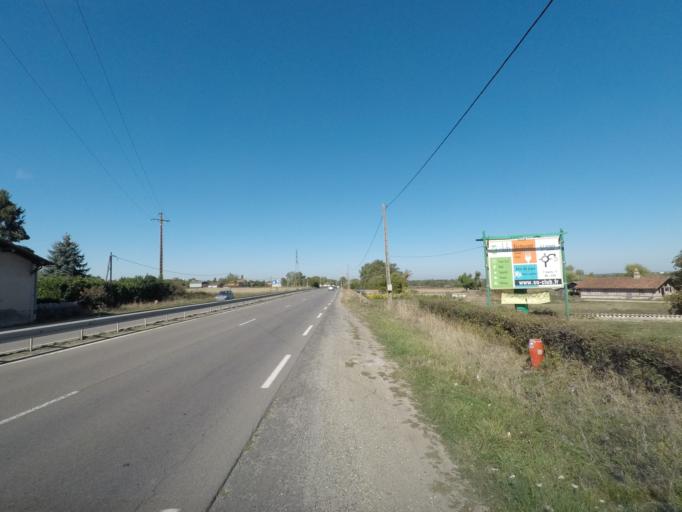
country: FR
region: Rhone-Alpes
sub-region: Departement de l'Ain
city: Viriat
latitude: 46.2290
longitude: 5.2032
